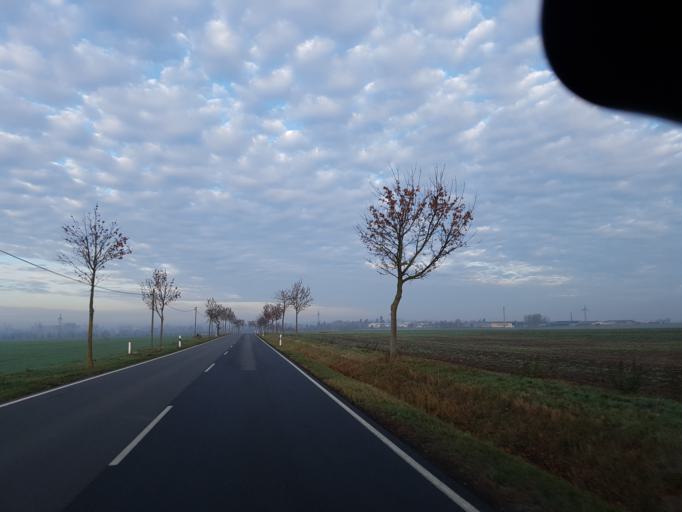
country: DE
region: Saxony-Anhalt
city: Zahna
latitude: 51.9051
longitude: 12.8127
